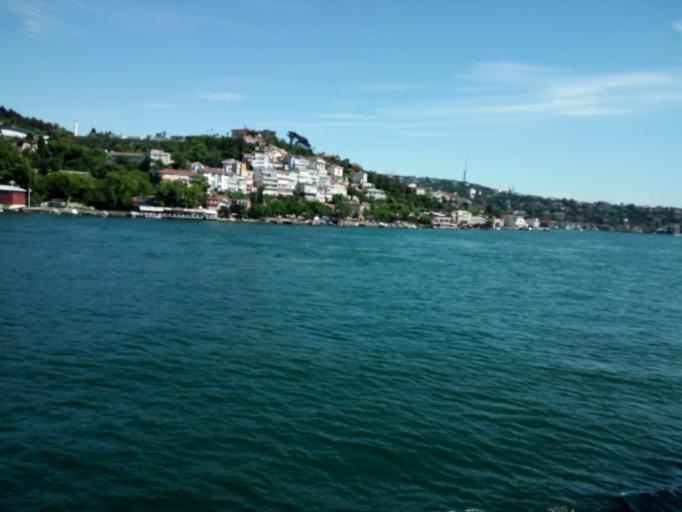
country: TR
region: Istanbul
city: UEskuedar
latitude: 41.0584
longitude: 29.0503
